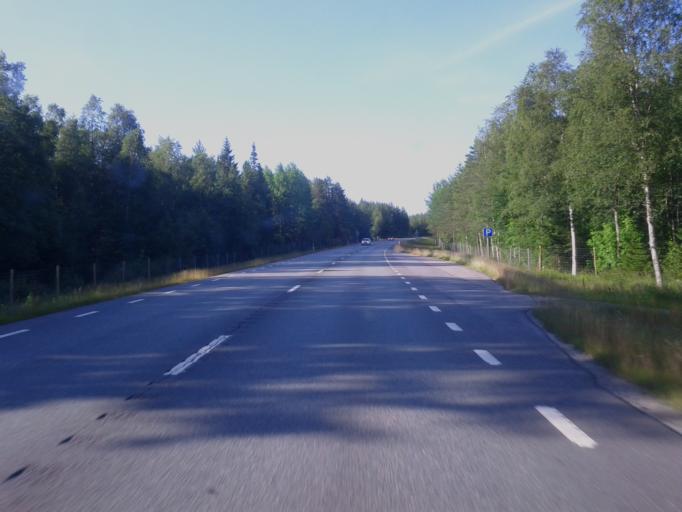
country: SE
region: Vaesterbotten
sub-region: Robertsfors Kommun
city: Robertsfors
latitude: 64.0341
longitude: 20.8420
